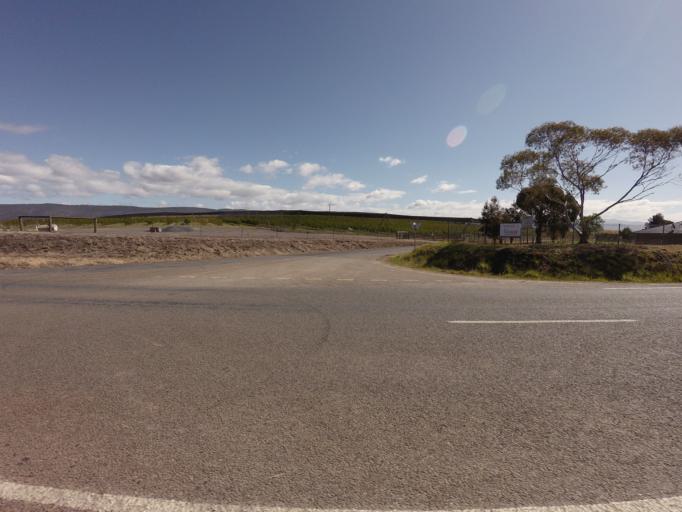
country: AU
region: Tasmania
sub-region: Derwent Valley
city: New Norfolk
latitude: -42.7093
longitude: 146.9461
